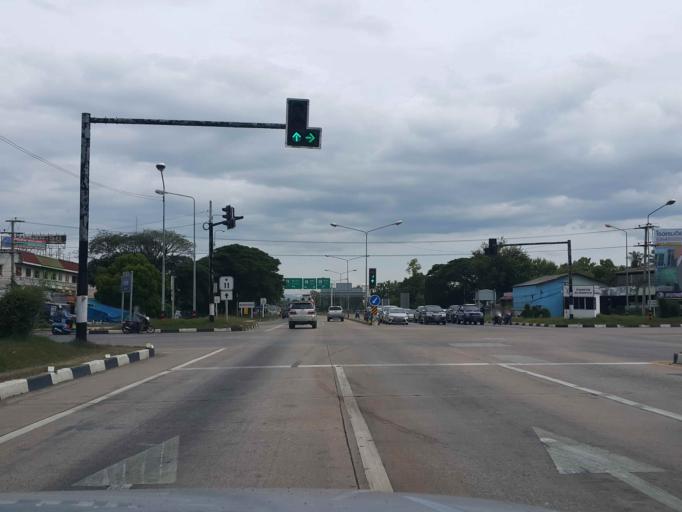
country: TH
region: Lampang
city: Lampang
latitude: 18.2674
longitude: 99.4654
